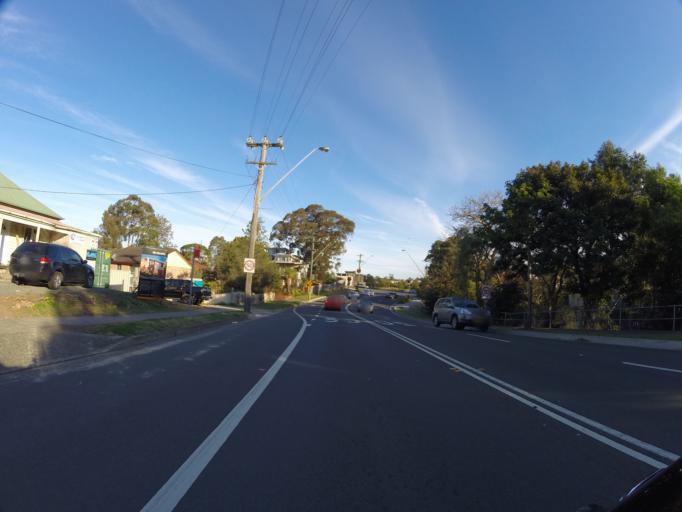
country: AU
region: New South Wales
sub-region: Wollongong
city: Bulli
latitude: -34.3187
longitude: 150.9167
